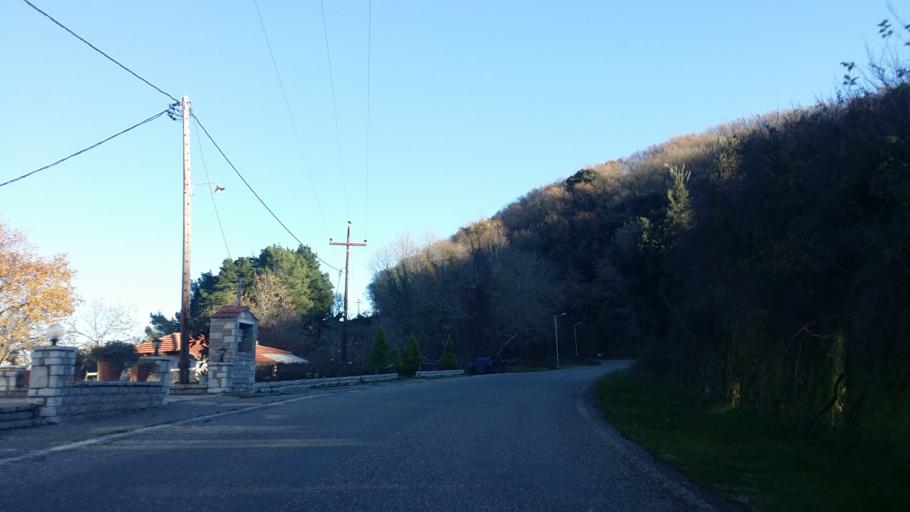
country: GR
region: West Greece
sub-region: Nomos Aitolias kai Akarnanias
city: Sardinia
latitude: 38.8662
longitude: 21.2901
